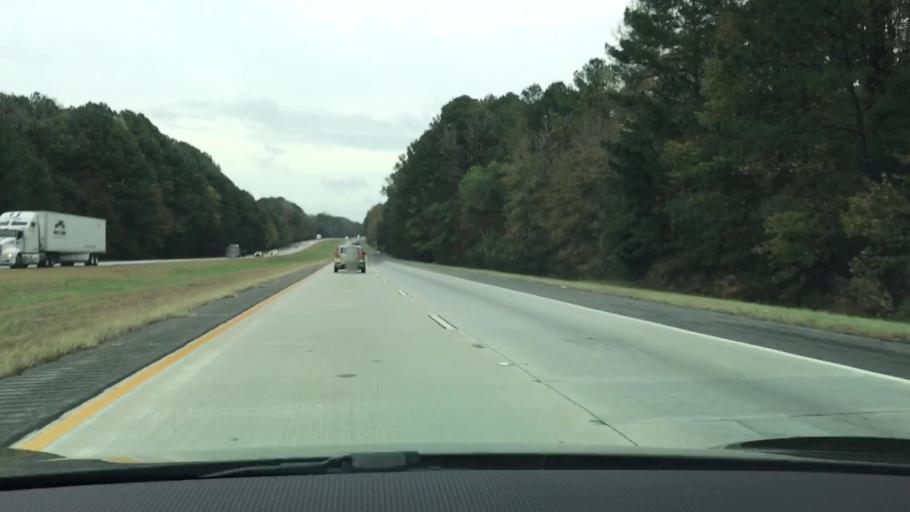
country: US
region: Georgia
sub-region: Greene County
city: Union Point
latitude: 33.5481
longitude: -83.0429
